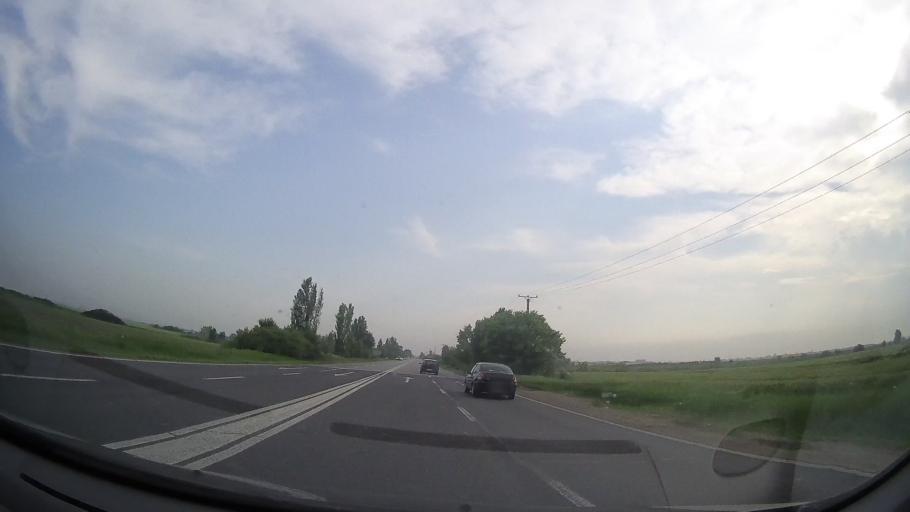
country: RO
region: Timis
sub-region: Comuna Sag
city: Sag
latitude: 45.6850
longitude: 21.1694
